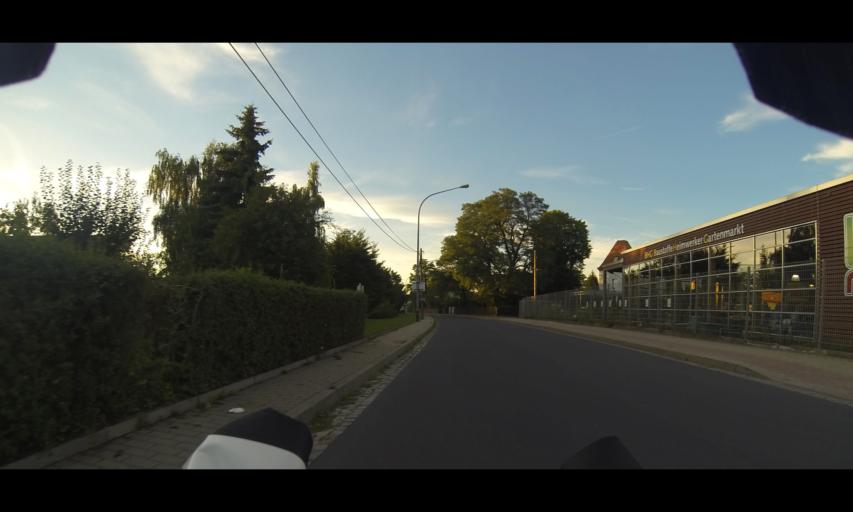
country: DE
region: Saxony
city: Radeburg
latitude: 51.2077
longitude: 13.7277
